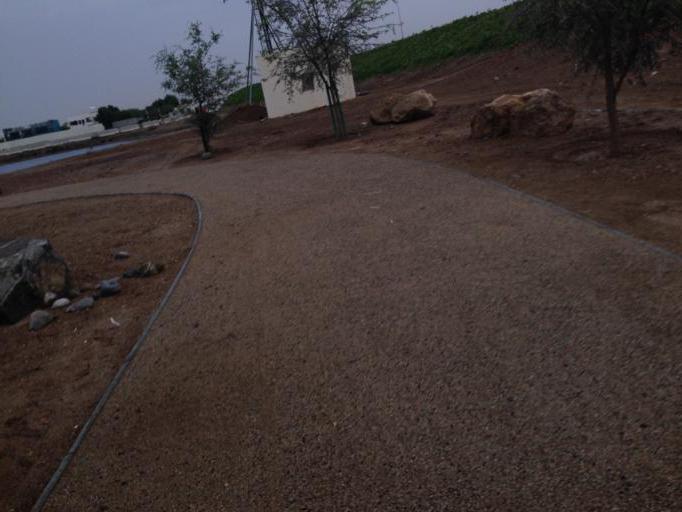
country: OM
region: Muhafazat Masqat
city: As Sib al Jadidah
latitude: 23.6214
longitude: 58.2720
